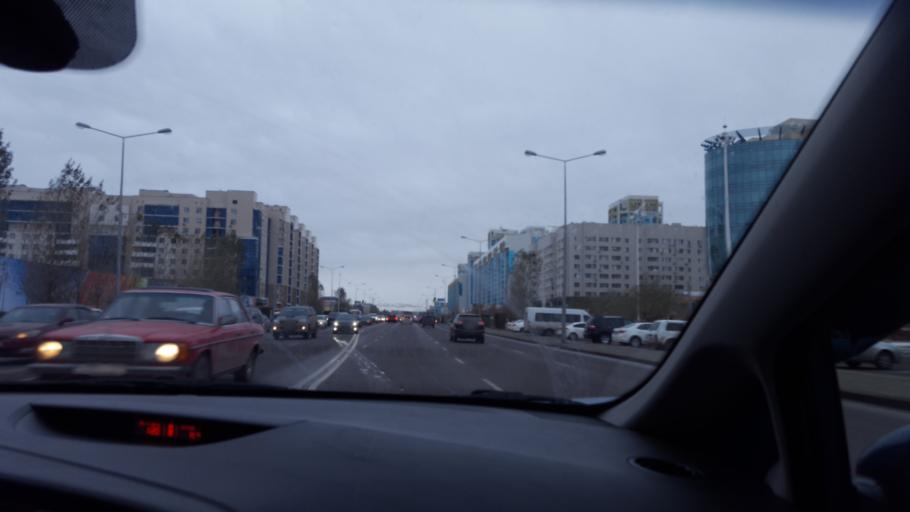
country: KZ
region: Astana Qalasy
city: Astana
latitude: 51.1335
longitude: 71.4333
